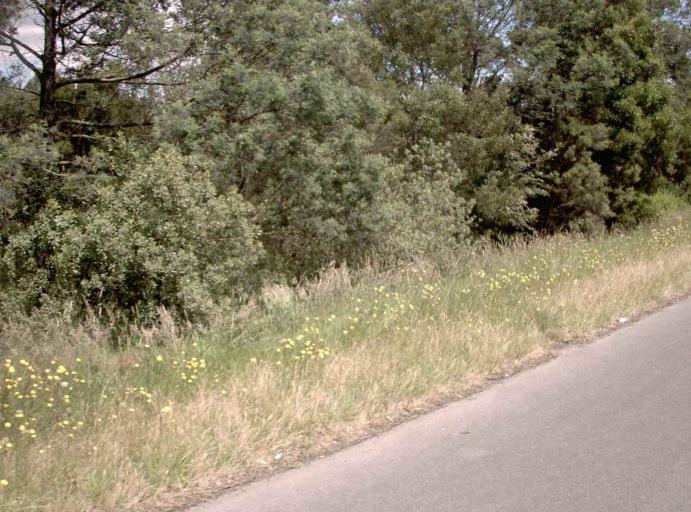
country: AU
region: Victoria
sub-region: Cardinia
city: Koo-Wee-Rup
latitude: -38.3360
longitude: 145.5555
